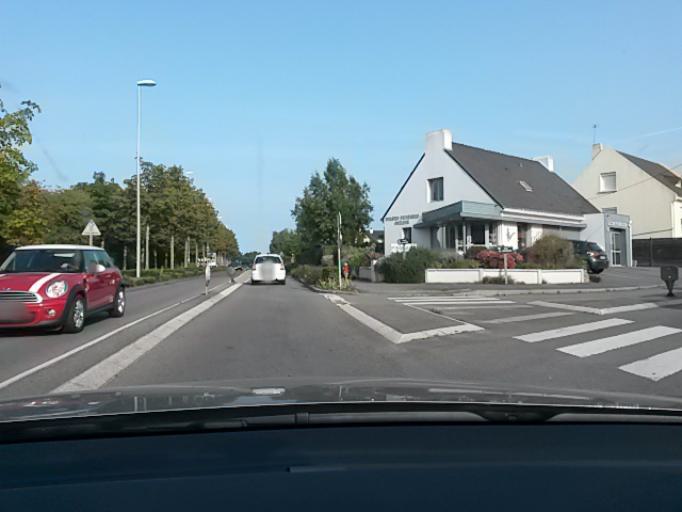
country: FR
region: Pays de la Loire
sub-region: Departement de la Loire-Atlantique
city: Guerande
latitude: 47.3293
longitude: -2.4221
